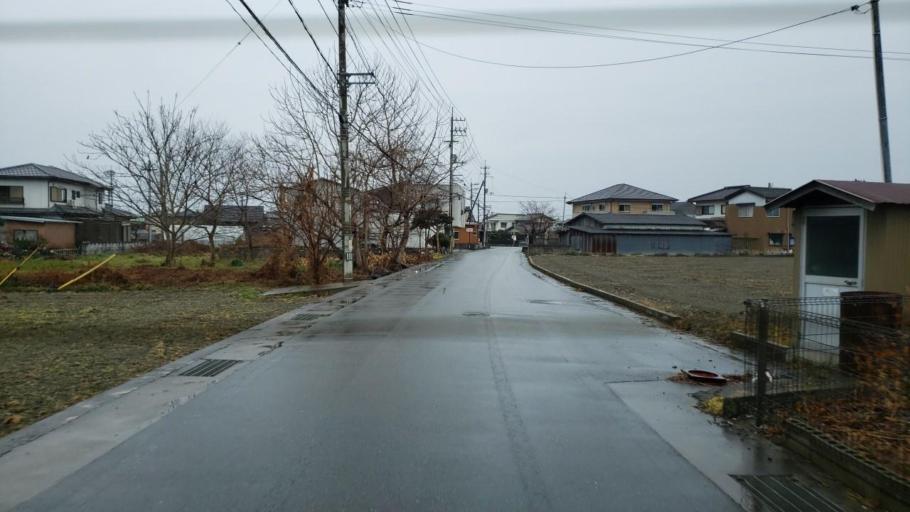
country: JP
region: Tokushima
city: Kamojimacho-jogejima
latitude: 34.0580
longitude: 134.2984
